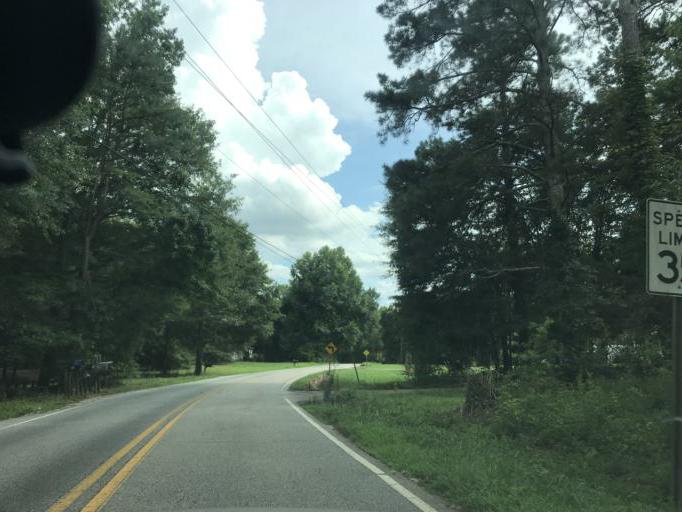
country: US
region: Georgia
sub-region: Forsyth County
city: Cumming
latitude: 34.2790
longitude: -84.1530
